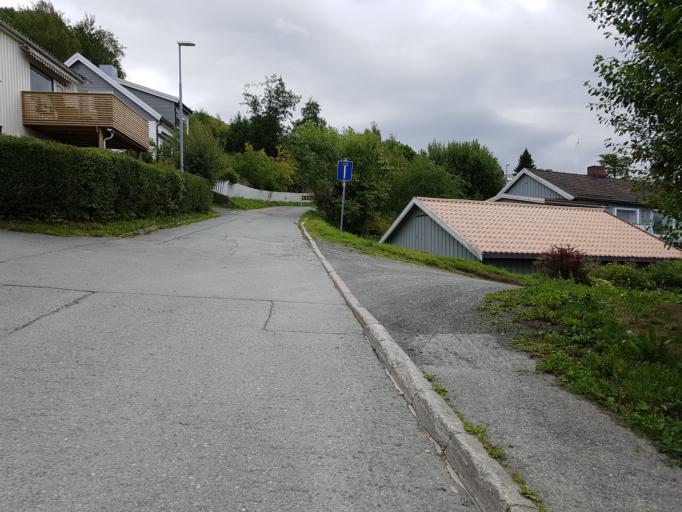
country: NO
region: Sor-Trondelag
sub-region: Trondheim
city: Trondheim
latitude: 63.3974
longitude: 10.4136
